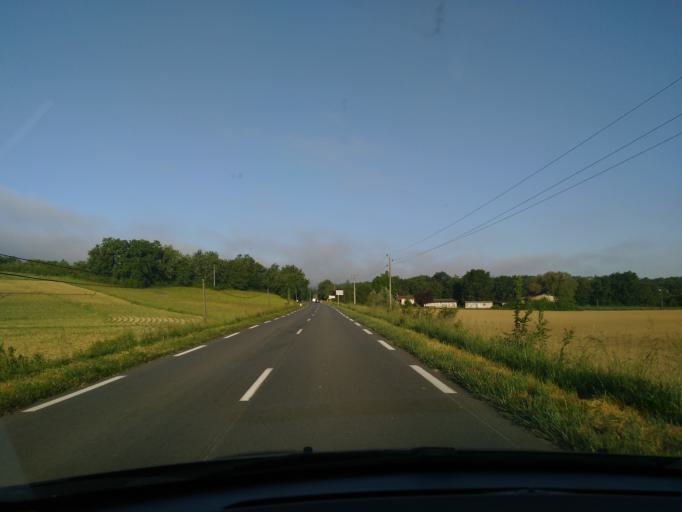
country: FR
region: Midi-Pyrenees
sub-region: Departement du Gers
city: Gondrin
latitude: 43.8778
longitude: 0.2084
